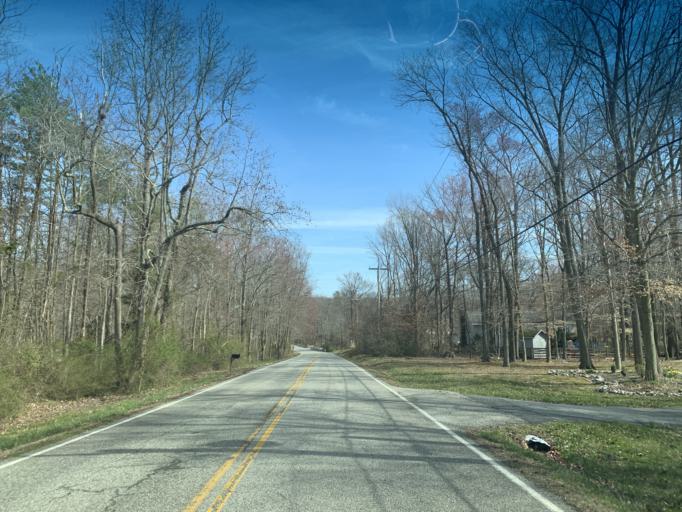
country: US
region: Maryland
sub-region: Cecil County
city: Charlestown
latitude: 39.5622
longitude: -76.0069
